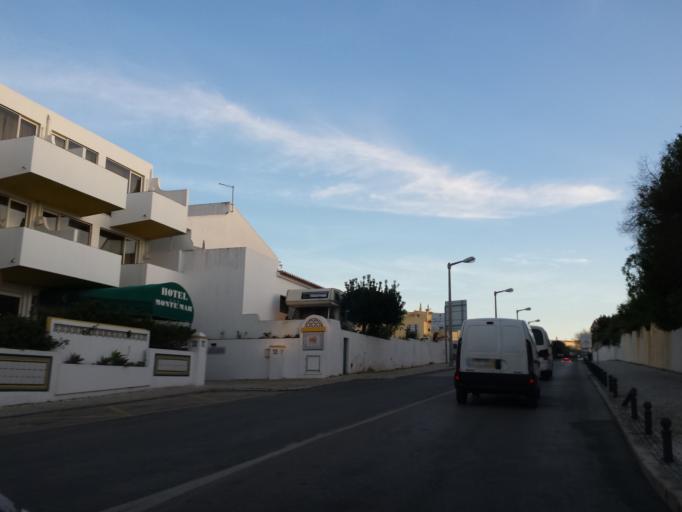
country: PT
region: Faro
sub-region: Lagos
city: Lagos
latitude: 37.0951
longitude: -8.6749
